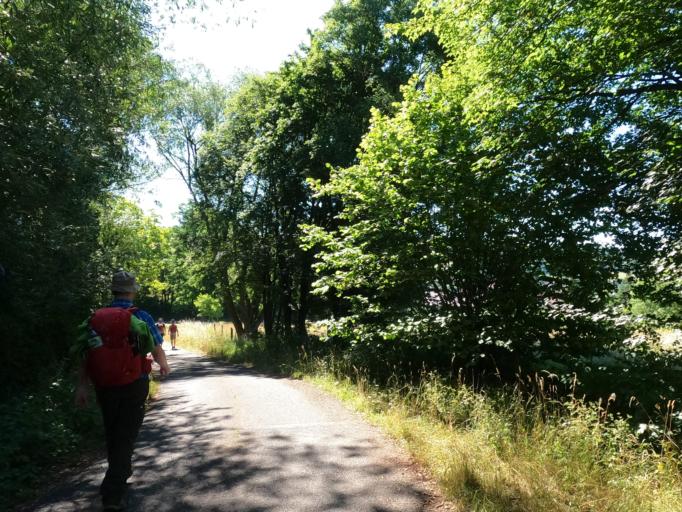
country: DE
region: Hesse
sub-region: Regierungsbezirk Darmstadt
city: Schluchtern
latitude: 50.3259
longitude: 9.5336
